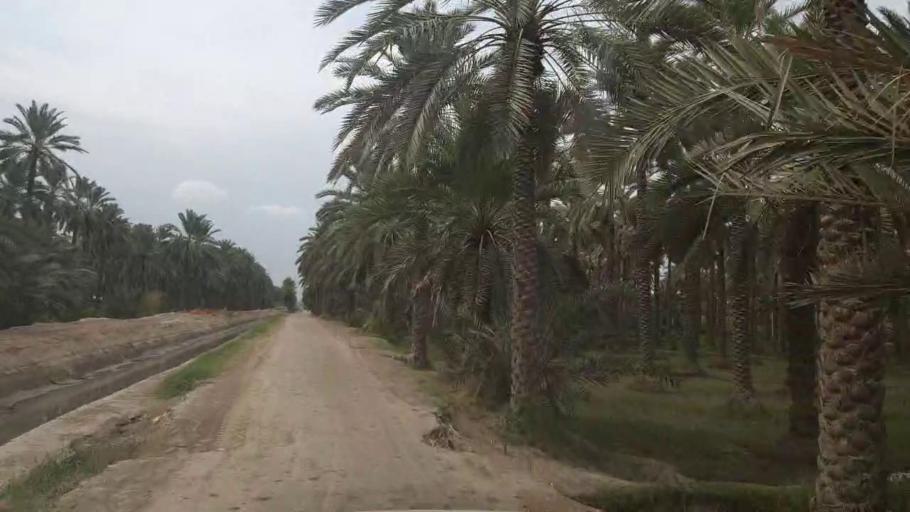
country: PK
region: Sindh
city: Sukkur
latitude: 27.6217
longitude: 68.8067
